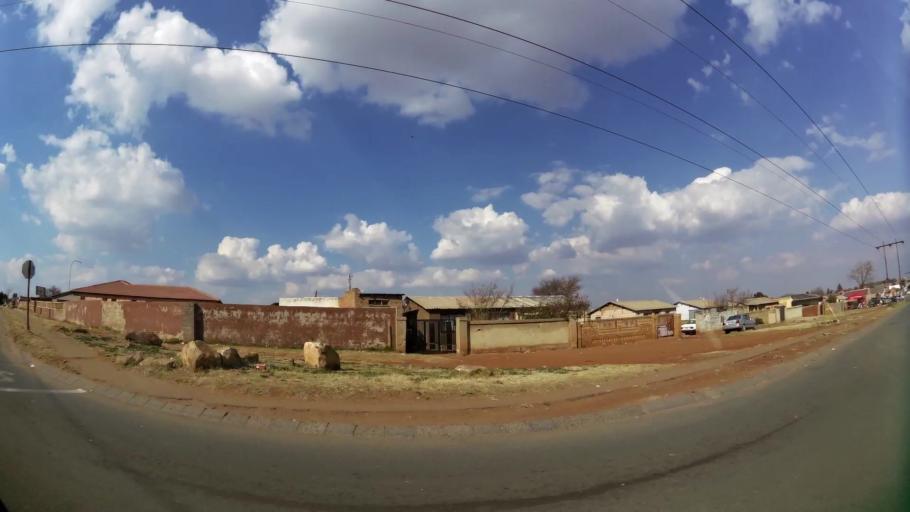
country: ZA
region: Gauteng
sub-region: City of Johannesburg Metropolitan Municipality
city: Soweto
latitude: -26.2179
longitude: 27.8578
